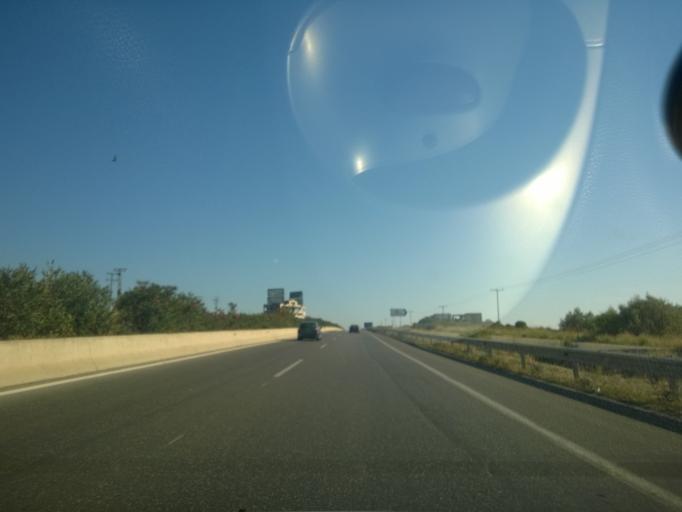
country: GR
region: Central Macedonia
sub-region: Nomos Chalkidikis
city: Lakkoma
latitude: 40.3579
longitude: 23.0538
